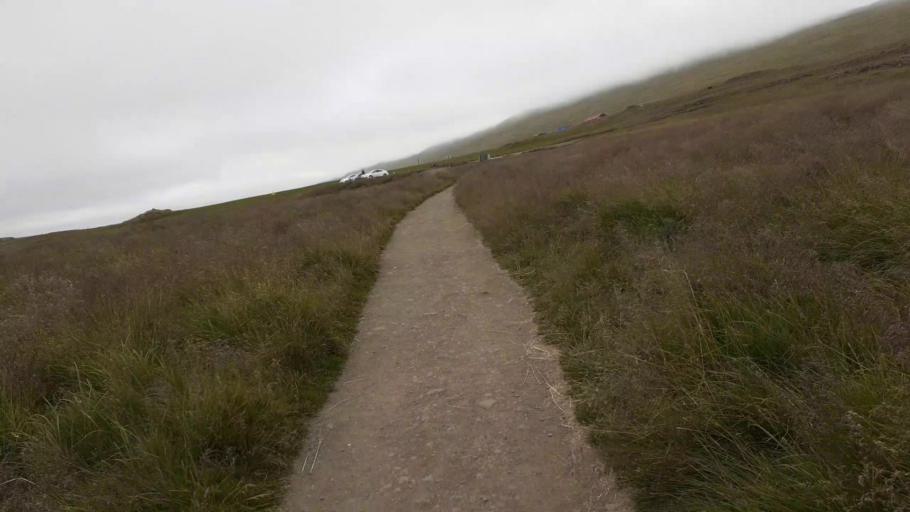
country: IS
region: Northwest
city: Saudarkrokur
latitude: 65.6047
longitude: -20.6387
